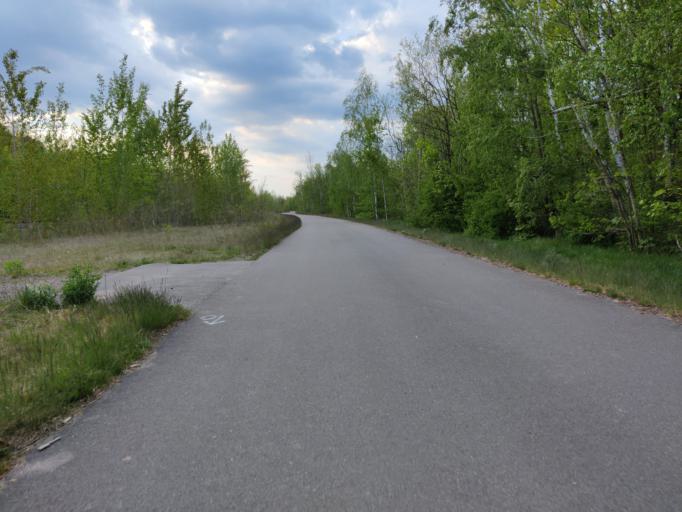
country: DE
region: Saxony
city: Rotha
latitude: 51.2090
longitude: 12.4449
